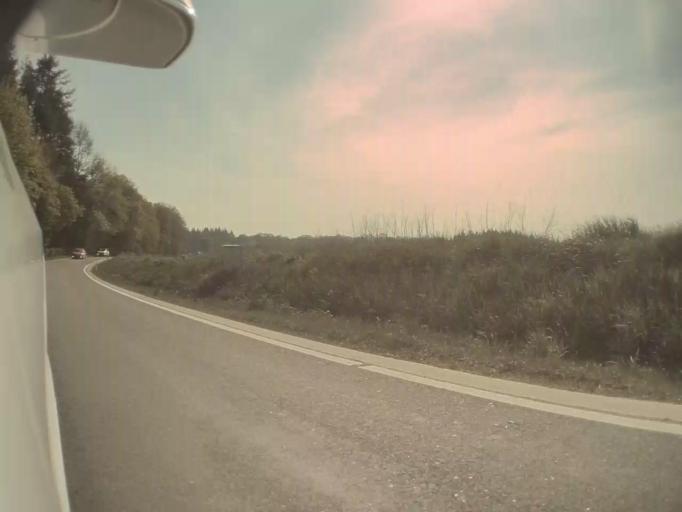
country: BE
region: Wallonia
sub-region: Province de Namur
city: Havelange
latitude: 50.3164
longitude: 5.2406
